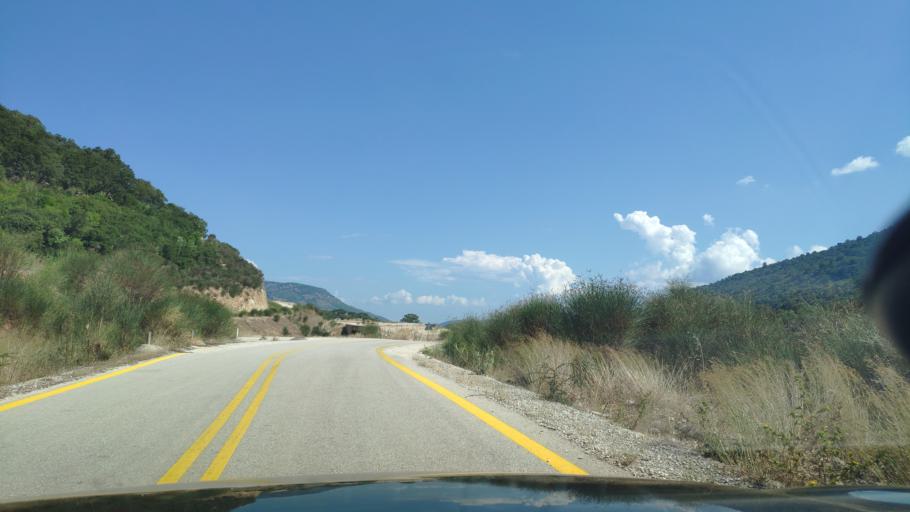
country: GR
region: West Greece
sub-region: Nomos Aitolias kai Akarnanias
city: Katouna
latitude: 38.8540
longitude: 21.0886
